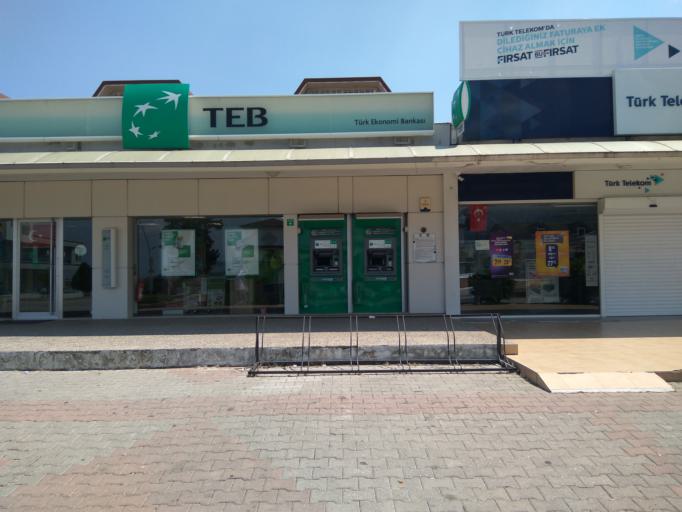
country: TR
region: Antalya
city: Kemer
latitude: 36.6007
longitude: 30.5538
